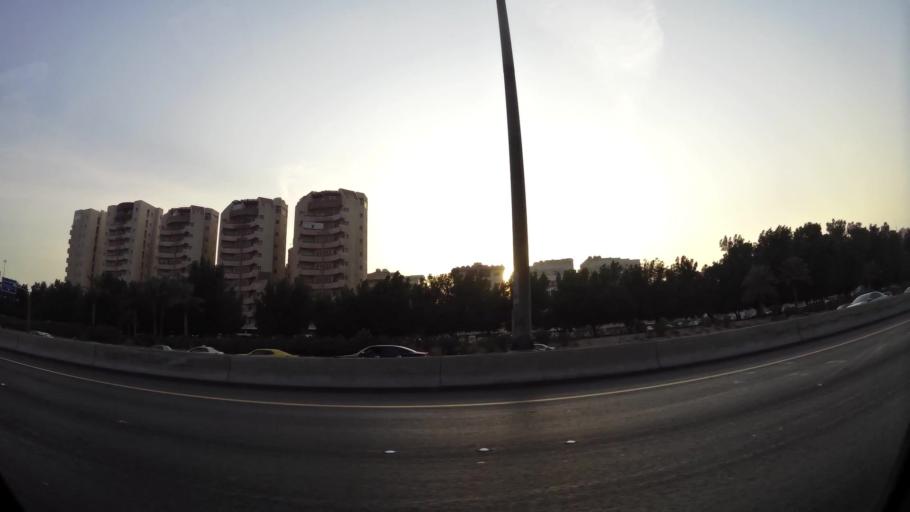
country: KW
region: Muhafazat Hawalli
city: Hawalli
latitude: 29.3339
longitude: 48.0380
